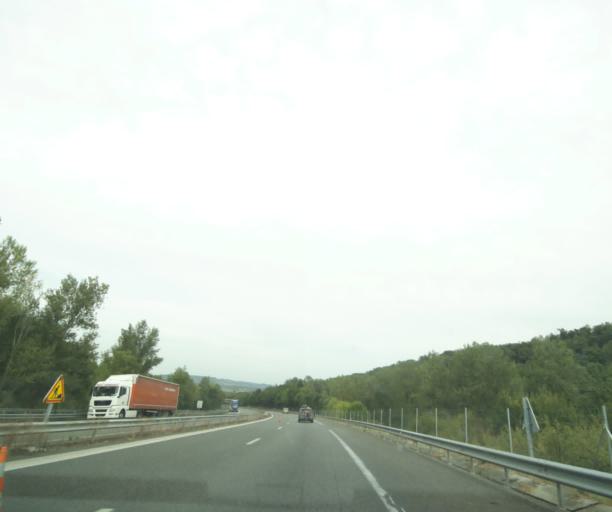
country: FR
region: Aquitaine
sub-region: Departement du Lot-et-Garonne
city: Layrac
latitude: 44.1405
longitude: 0.6407
